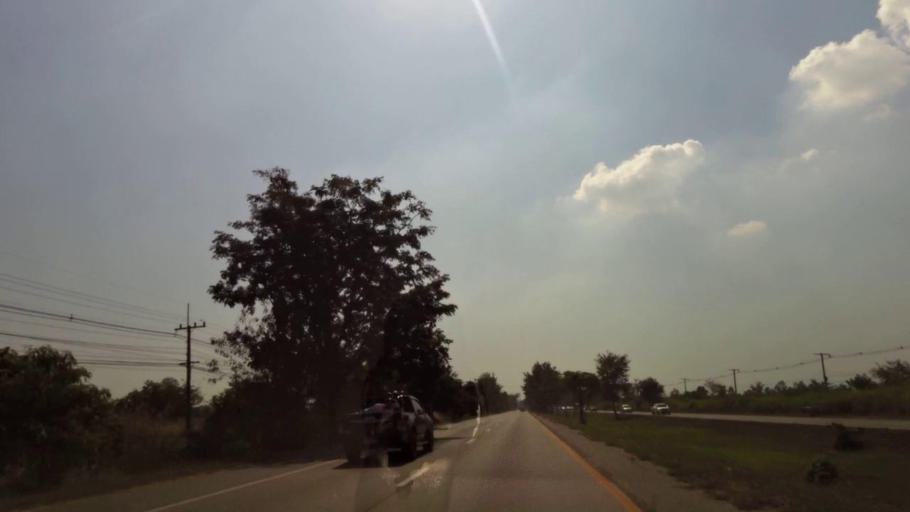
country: TH
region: Phichit
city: Wachira Barami
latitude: 16.5433
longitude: 100.1454
